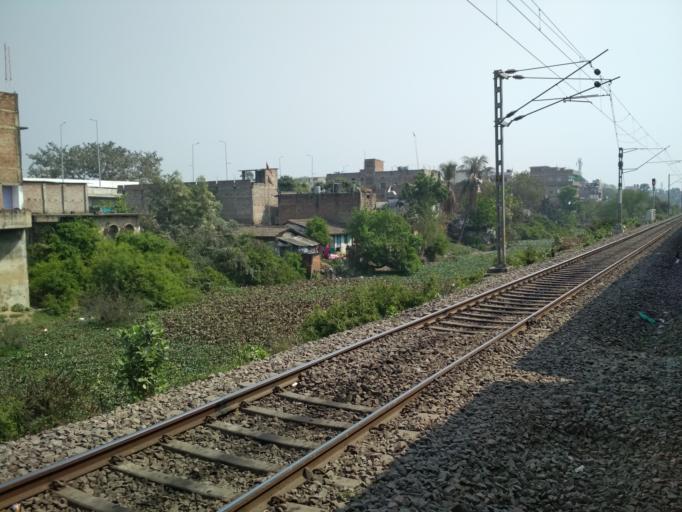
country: IN
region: Bihar
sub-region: Khagaria
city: Khagaria
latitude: 25.5066
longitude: 86.4739
